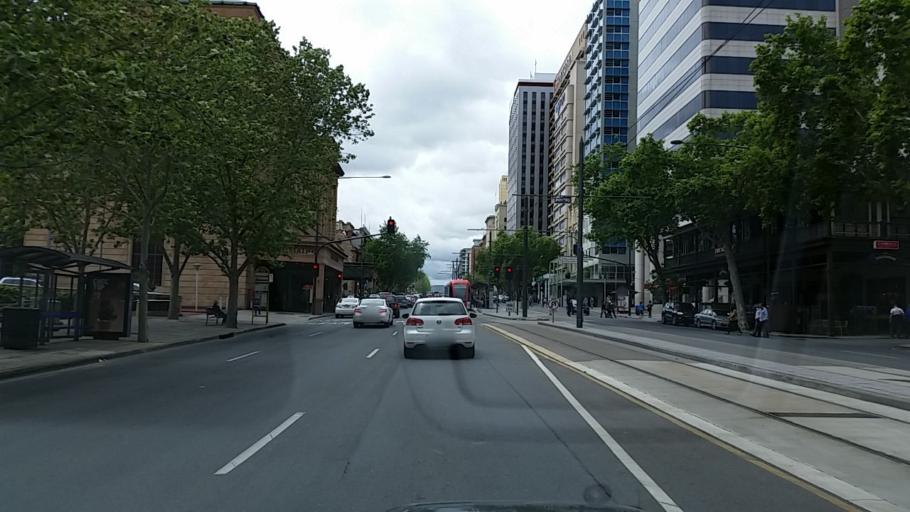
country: AU
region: South Australia
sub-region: Adelaide
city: Adelaide
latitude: -34.9217
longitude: 138.5964
